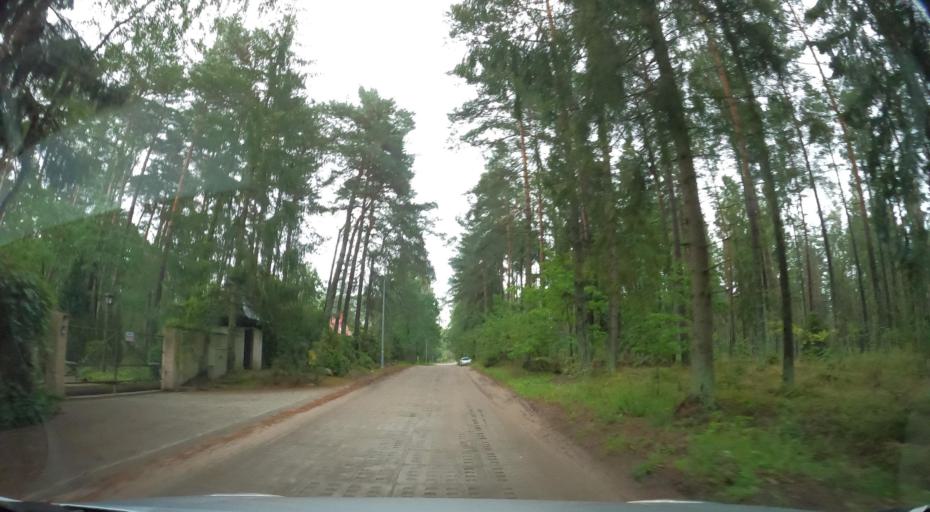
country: PL
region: Pomeranian Voivodeship
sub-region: Powiat kartuski
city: Chwaszczyno
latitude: 54.4183
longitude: 18.4288
